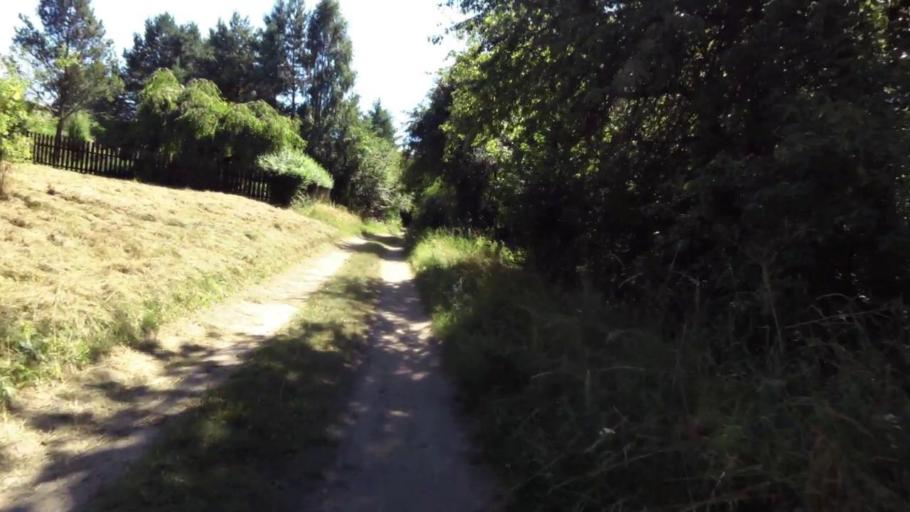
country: PL
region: West Pomeranian Voivodeship
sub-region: Powiat szczecinecki
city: Bialy Bor
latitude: 53.8369
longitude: 16.8744
